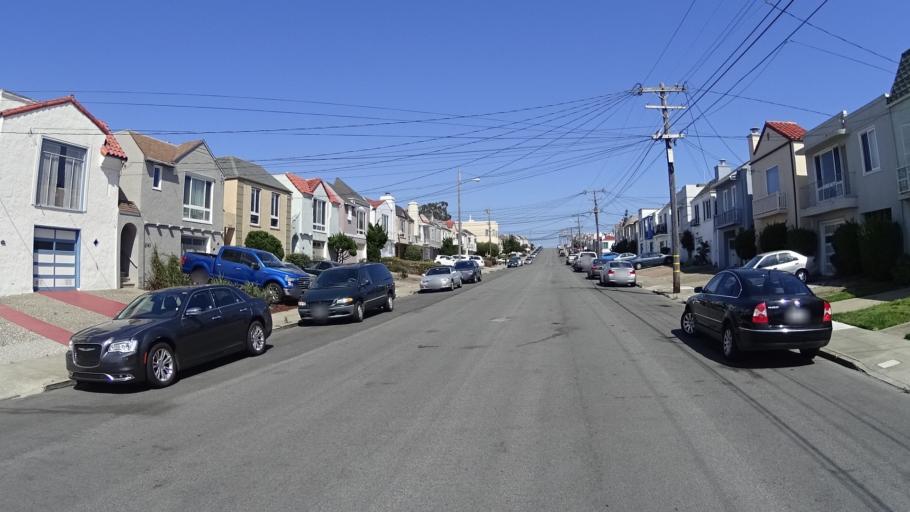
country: US
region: California
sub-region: San Mateo County
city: Daly City
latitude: 37.7470
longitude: -122.4888
